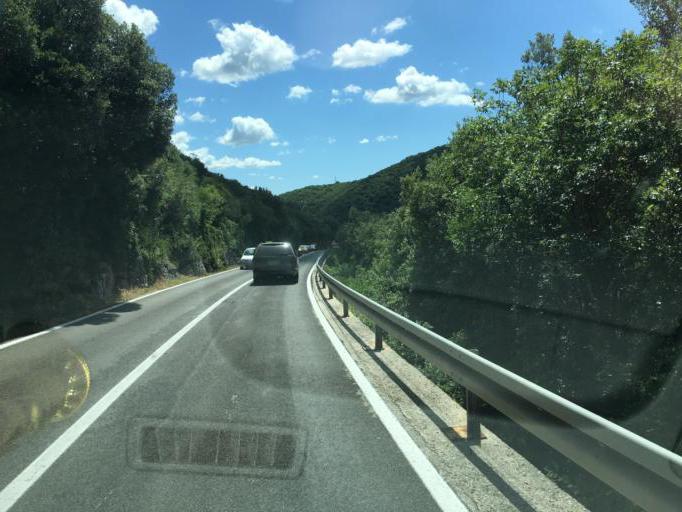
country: HR
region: Istarska
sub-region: Grad Rovinj
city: Rovinj
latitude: 45.1353
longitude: 13.7314
